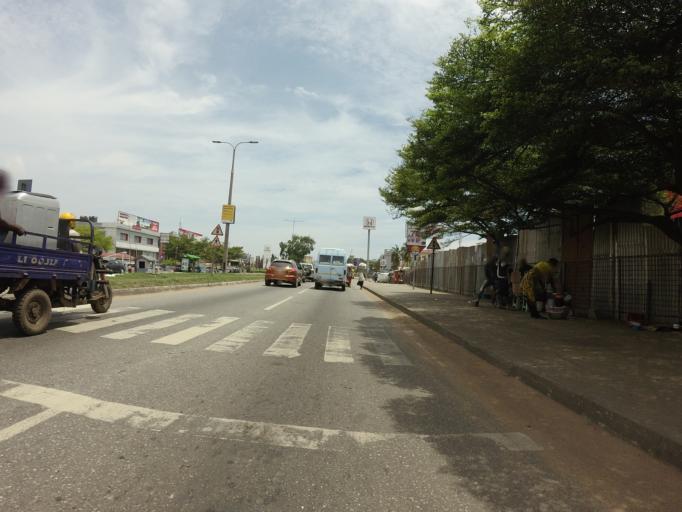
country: GH
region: Greater Accra
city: Accra
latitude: 5.5581
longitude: -0.2241
